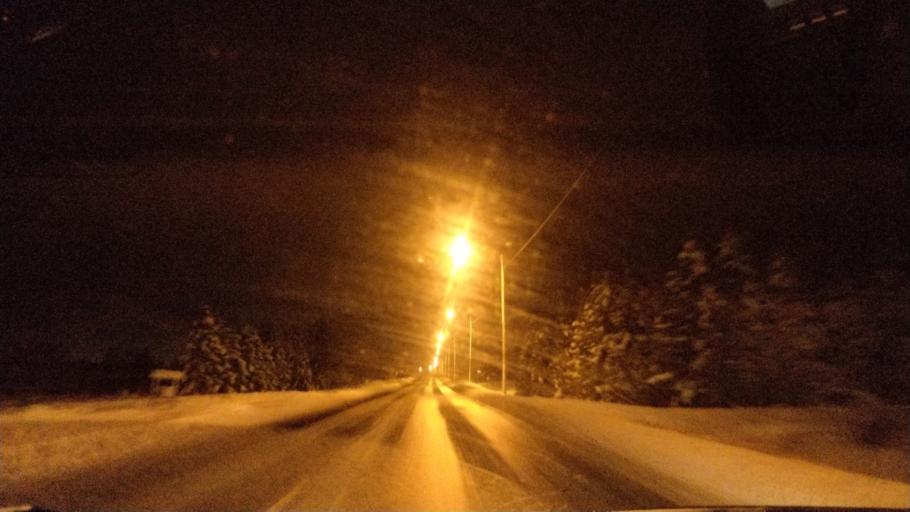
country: FI
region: Lapland
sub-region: Rovaniemi
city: Rovaniemi
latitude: 66.3962
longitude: 25.3845
